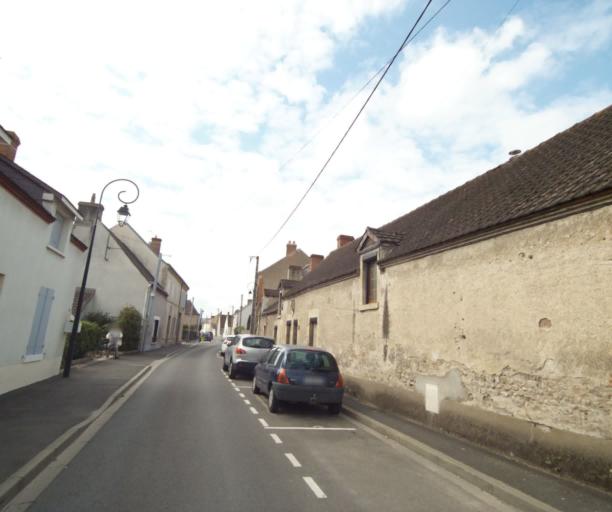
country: FR
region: Centre
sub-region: Departement du Loiret
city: Checy
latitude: 47.8960
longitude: 2.0250
